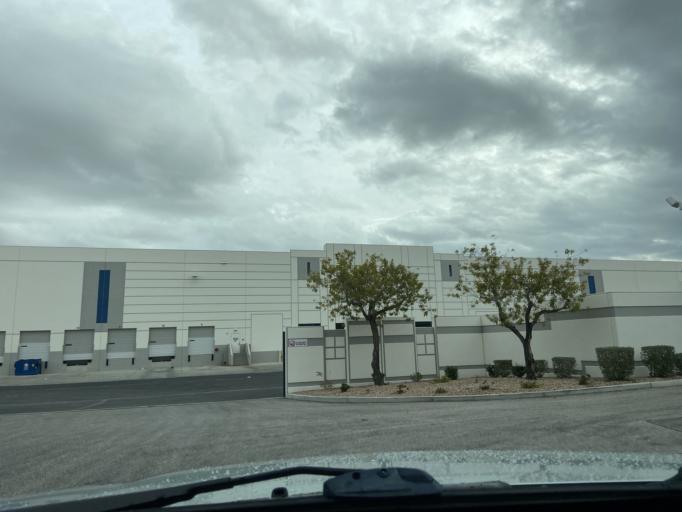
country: US
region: Nevada
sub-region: Clark County
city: North Las Vegas
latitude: 36.2419
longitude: -115.1077
